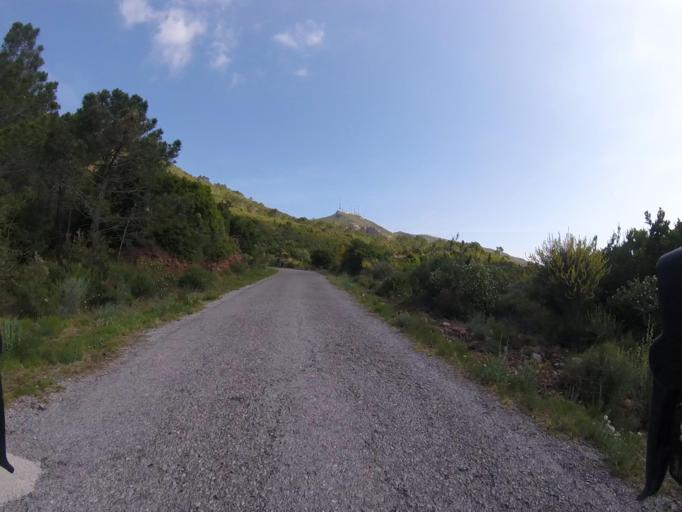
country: ES
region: Valencia
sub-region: Provincia de Castello
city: Benicassim
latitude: 40.0768
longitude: 0.0258
